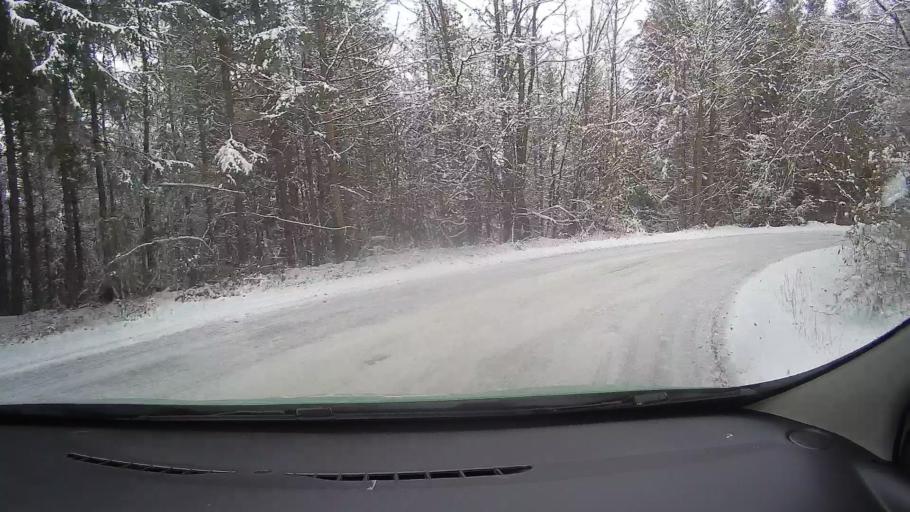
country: RO
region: Alba
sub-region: Comuna Almasu Mare
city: Almasu Mare
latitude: 46.0970
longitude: 23.1481
